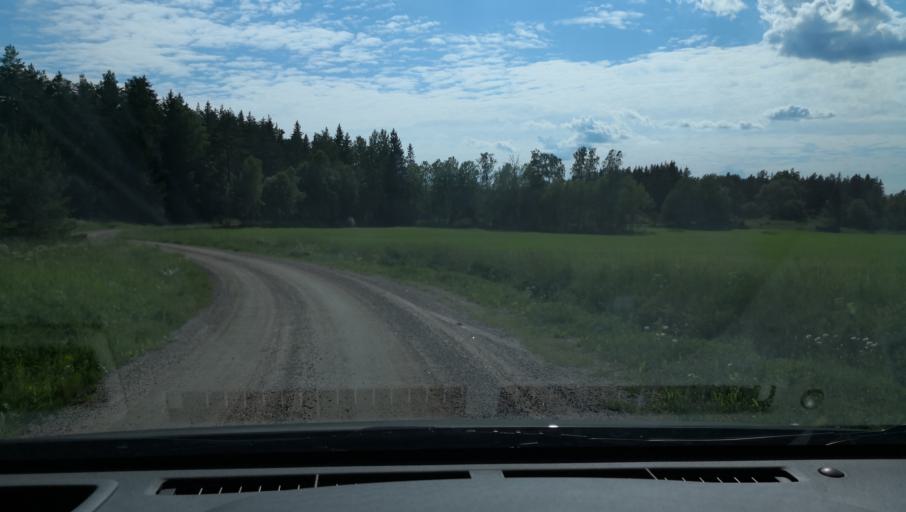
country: SE
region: Uppsala
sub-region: Enkopings Kommun
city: Orsundsbro
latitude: 59.8350
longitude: 17.2486
